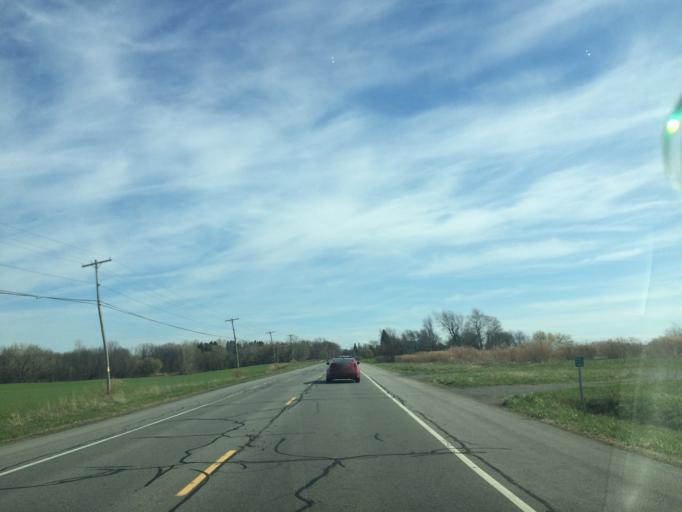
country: US
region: New York
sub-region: Monroe County
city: Webster
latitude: 43.1657
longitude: -77.4314
